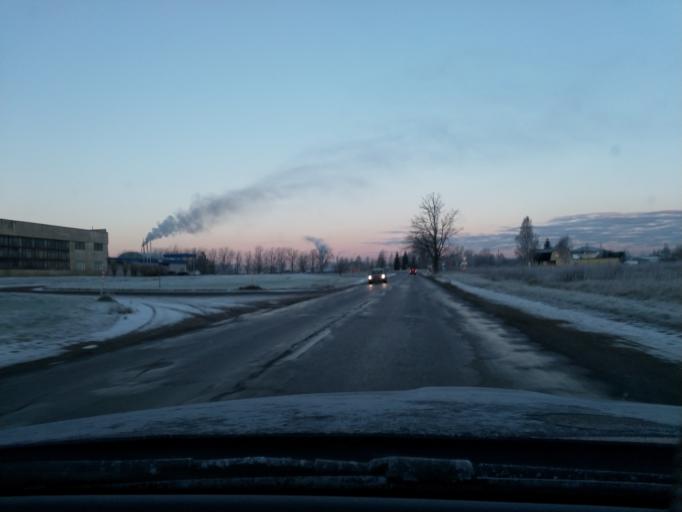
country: LV
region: Kuldigas Rajons
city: Kuldiga
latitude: 56.9548
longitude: 21.9911
